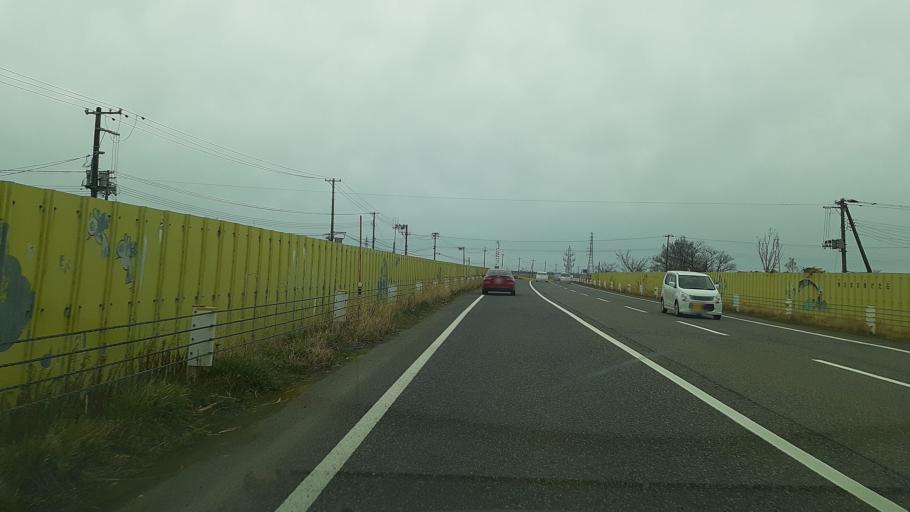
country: JP
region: Niigata
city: Niitsu-honcho
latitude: 37.7982
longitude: 139.1056
